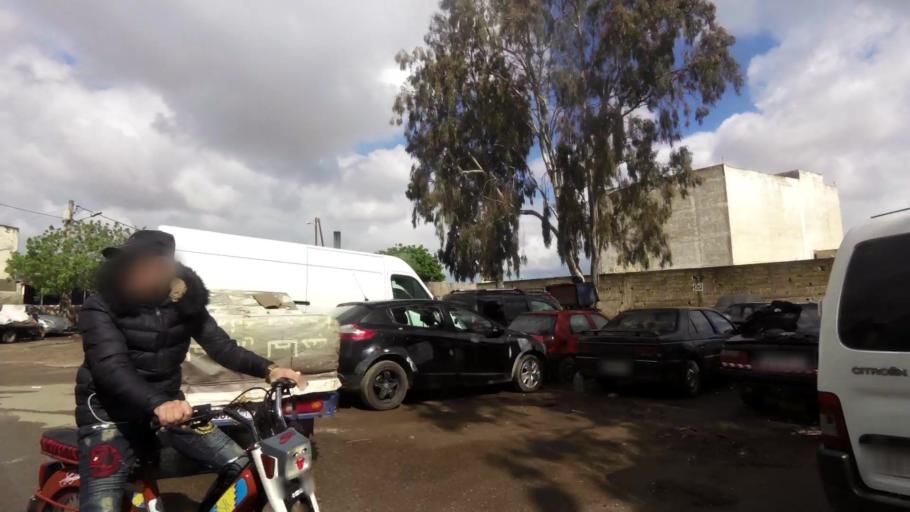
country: MA
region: Grand Casablanca
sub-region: Casablanca
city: Casablanca
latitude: 33.5331
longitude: -7.6684
